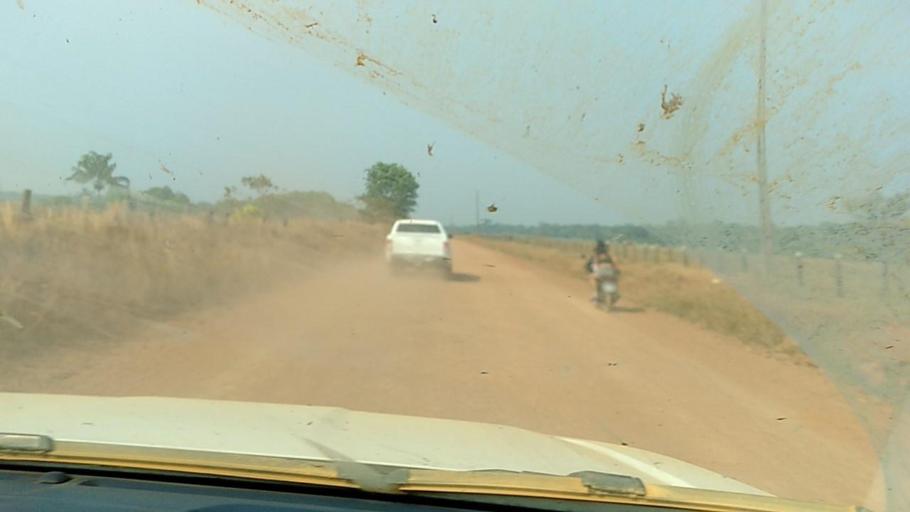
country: BR
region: Rondonia
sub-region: Porto Velho
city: Porto Velho
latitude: -8.7754
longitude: -64.0823
